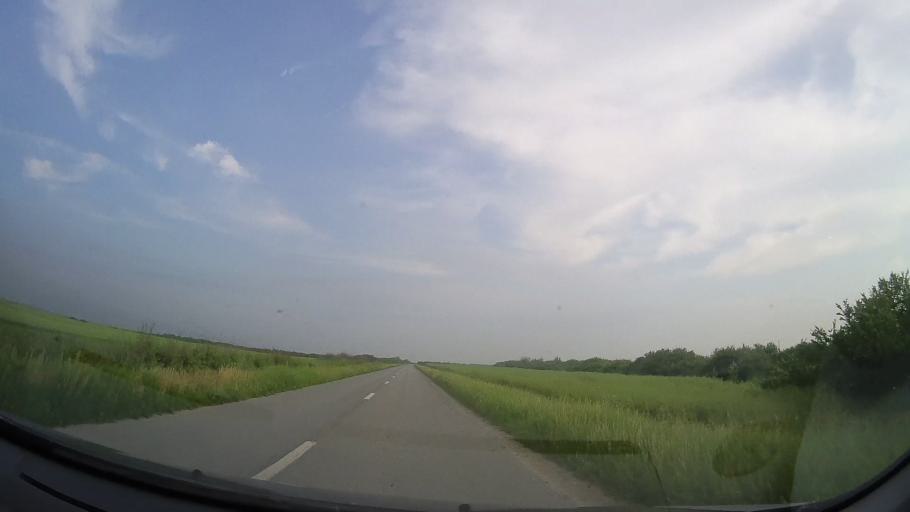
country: RS
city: Jasa Tomic
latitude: 45.4810
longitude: 20.8451
